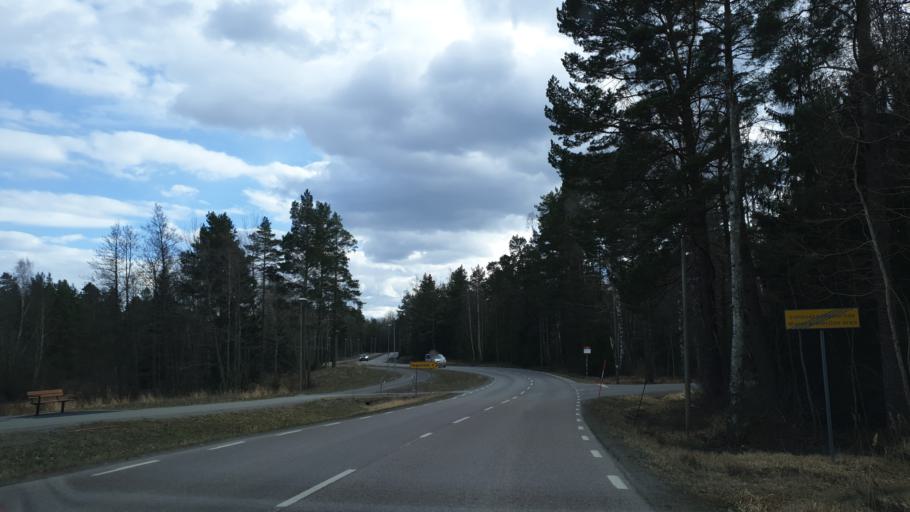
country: SE
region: Stockholm
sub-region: Varmdo Kommun
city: Mortnas
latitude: 59.2737
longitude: 18.4252
